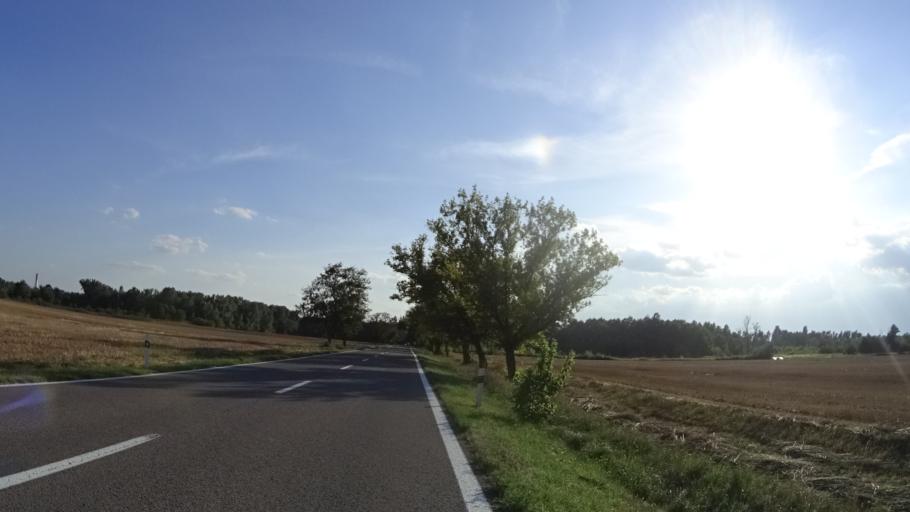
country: HU
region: Komarom-Esztergom
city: Nyergesujfalu
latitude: 47.7810
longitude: 18.5740
